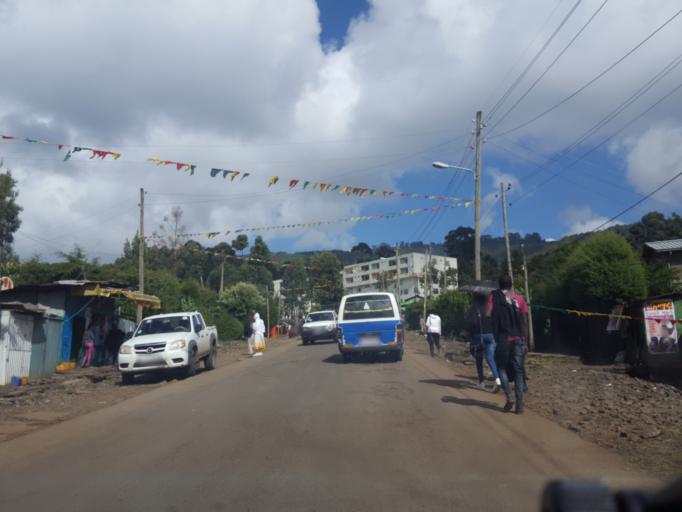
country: ET
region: Adis Abeba
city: Addis Ababa
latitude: 9.0722
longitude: 38.7596
